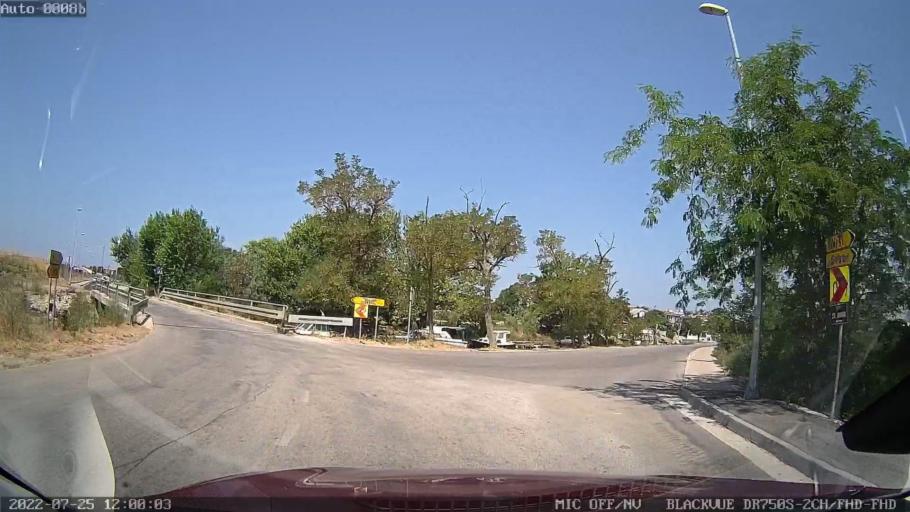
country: HR
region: Zadarska
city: Nin
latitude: 44.2432
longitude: 15.1963
